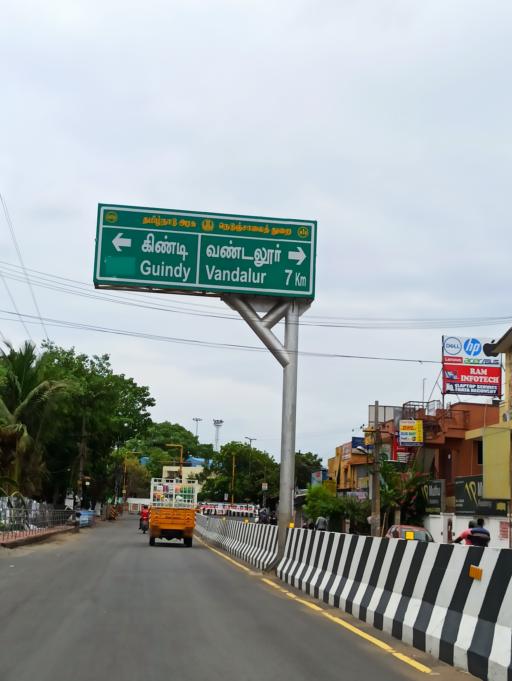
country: IN
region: Tamil Nadu
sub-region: Kancheepuram
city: Pallavaram
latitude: 12.9303
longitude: 80.1200
